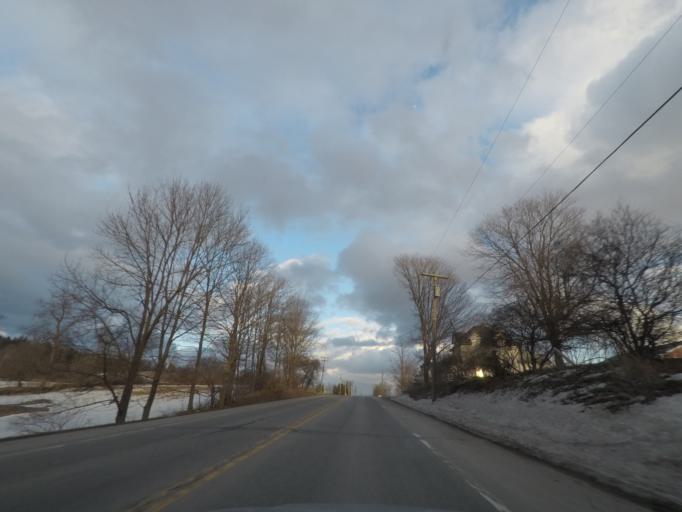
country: US
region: New York
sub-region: Montgomery County
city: Saint Johnsville
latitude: 43.0052
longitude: -74.7252
